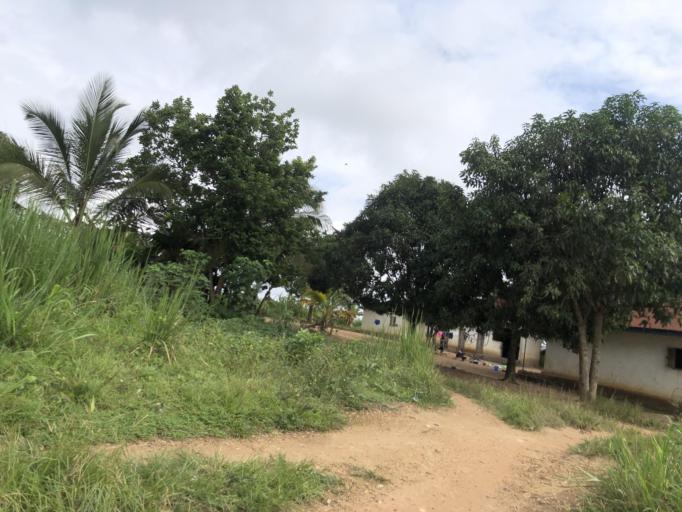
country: SL
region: Eastern Province
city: Kailahun
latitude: 8.2764
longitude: -10.5642
